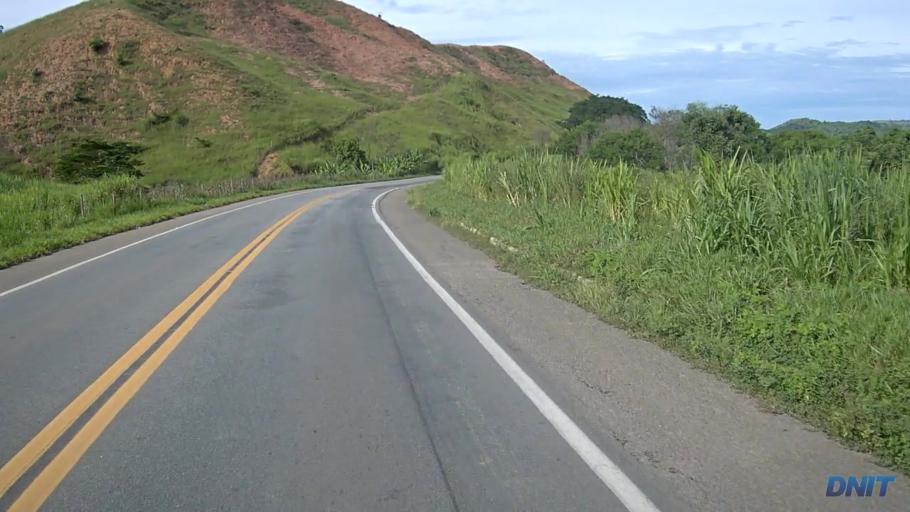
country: BR
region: Minas Gerais
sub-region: Belo Oriente
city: Belo Oriente
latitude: -19.1744
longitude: -42.2538
